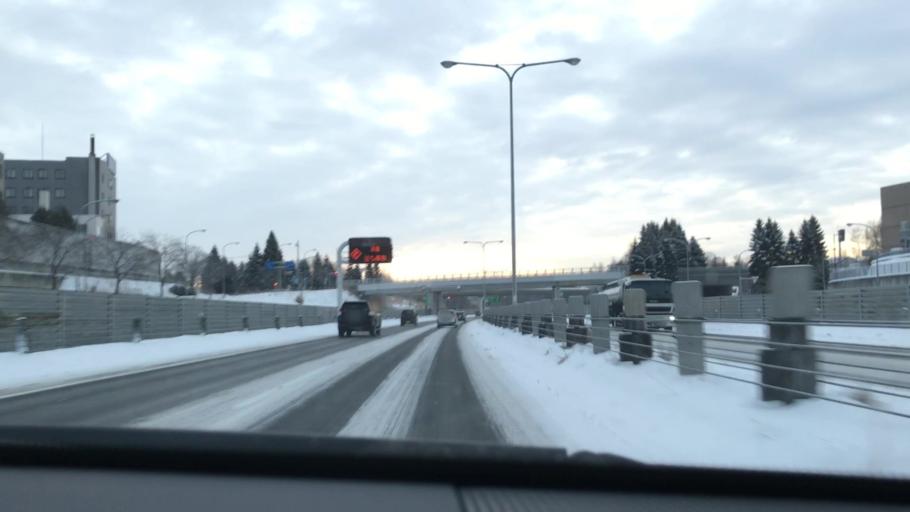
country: JP
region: Hokkaido
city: Sapporo
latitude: 43.0229
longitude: 141.4565
